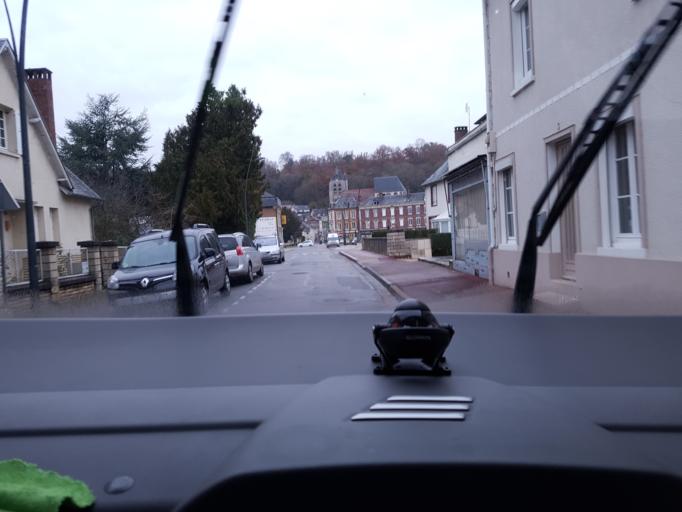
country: FR
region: Haute-Normandie
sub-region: Departement de l'Eure
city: Beaumont-le-Roger
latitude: 49.0792
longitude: 0.7763
